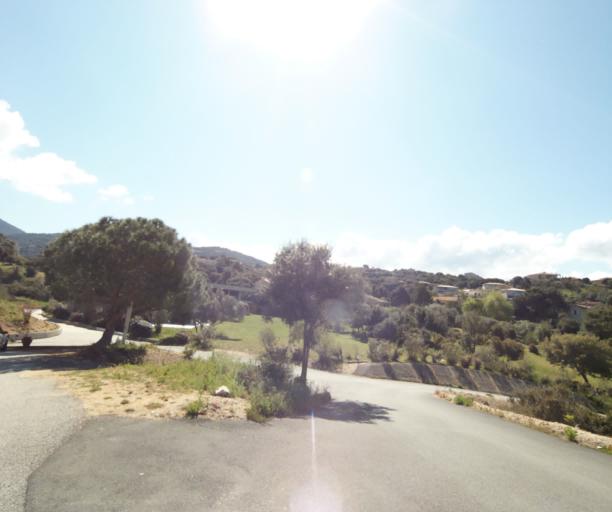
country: FR
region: Corsica
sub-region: Departement de la Corse-du-Sud
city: Propriano
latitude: 41.6795
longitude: 8.9165
